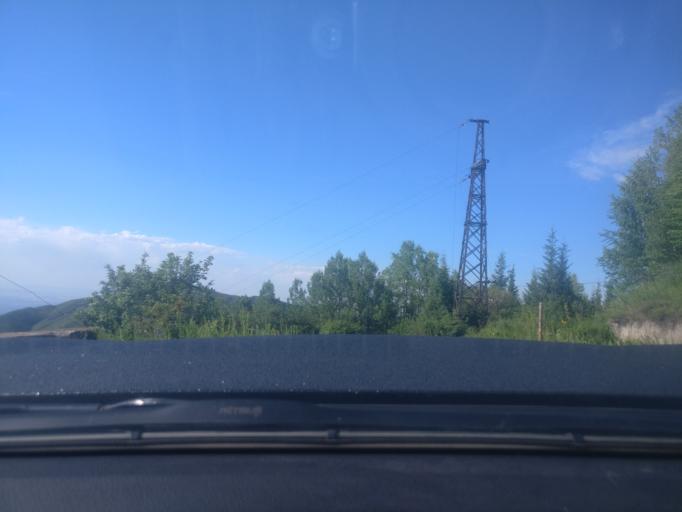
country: KZ
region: Almaty Qalasy
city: Almaty
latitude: 43.1157
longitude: 76.9287
